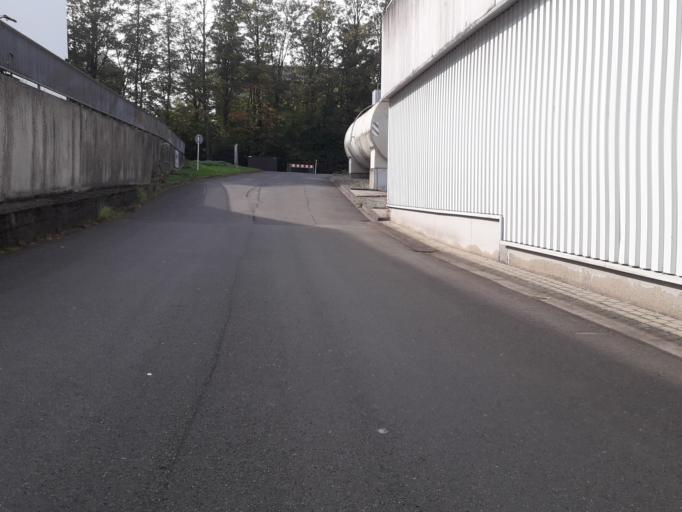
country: DE
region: North Rhine-Westphalia
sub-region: Regierungsbezirk Detmold
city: Paderborn
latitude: 51.7024
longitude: 8.7679
